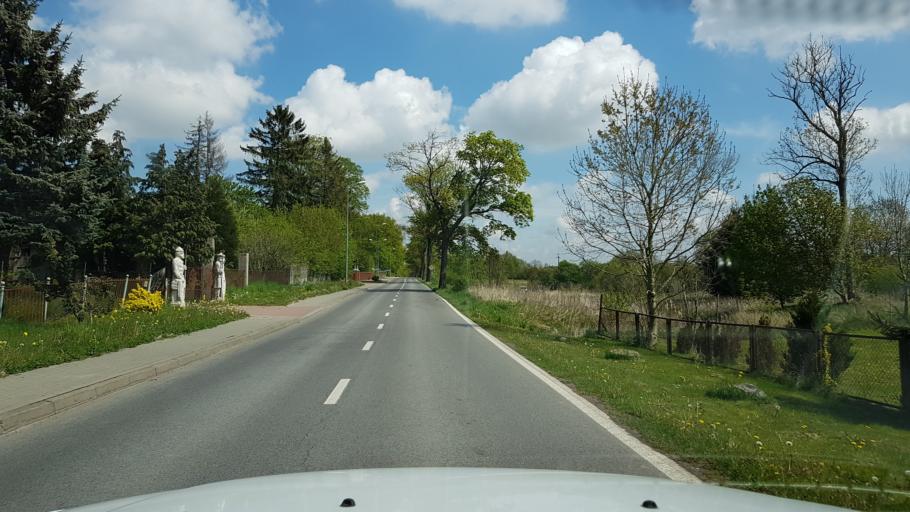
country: PL
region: West Pomeranian Voivodeship
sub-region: Powiat slawienski
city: Slawno
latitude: 54.4845
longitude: 16.6967
